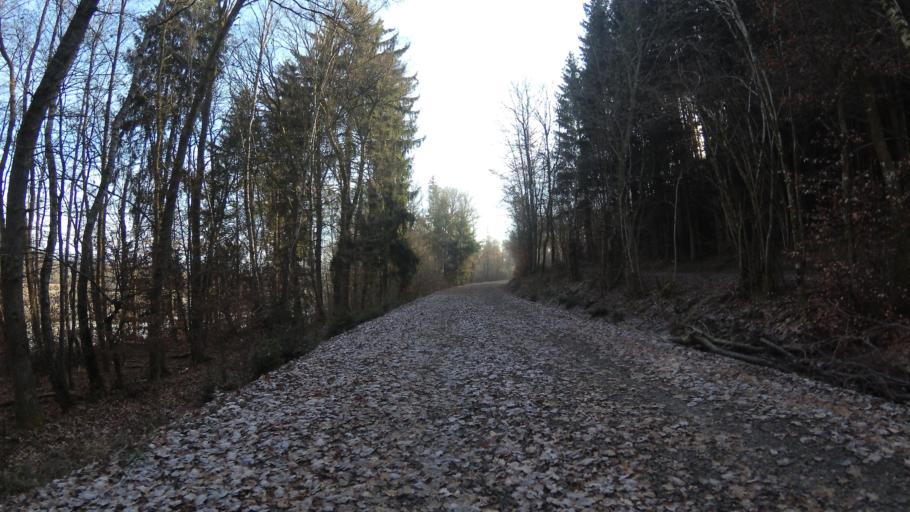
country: DE
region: Saarland
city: Nohfelden
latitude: 49.5753
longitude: 7.1584
